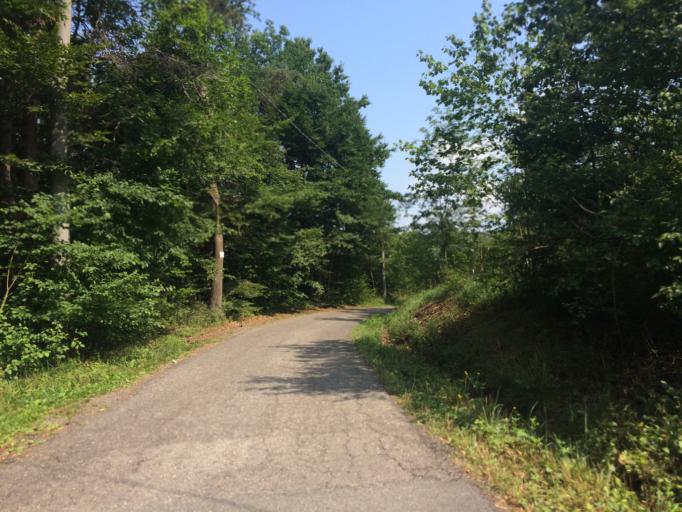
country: IT
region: Liguria
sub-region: Provincia di Savona
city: Piana Crixia
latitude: 44.4680
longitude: 8.3488
